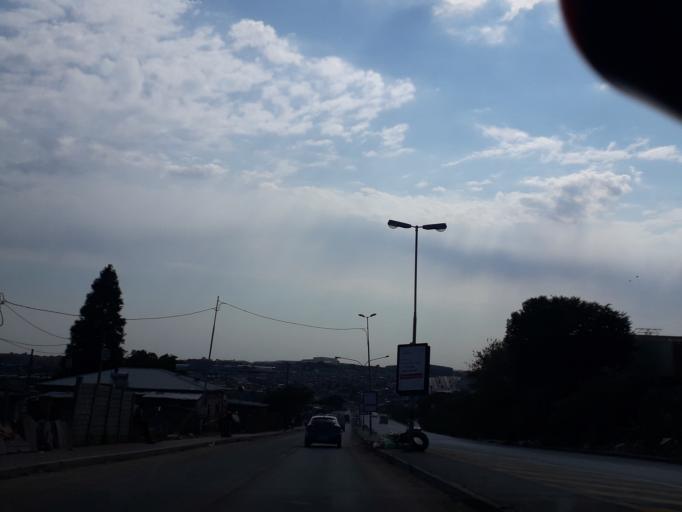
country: ZA
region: Gauteng
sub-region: City of Johannesburg Metropolitan Municipality
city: Modderfontein
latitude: -26.1128
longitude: 28.1031
